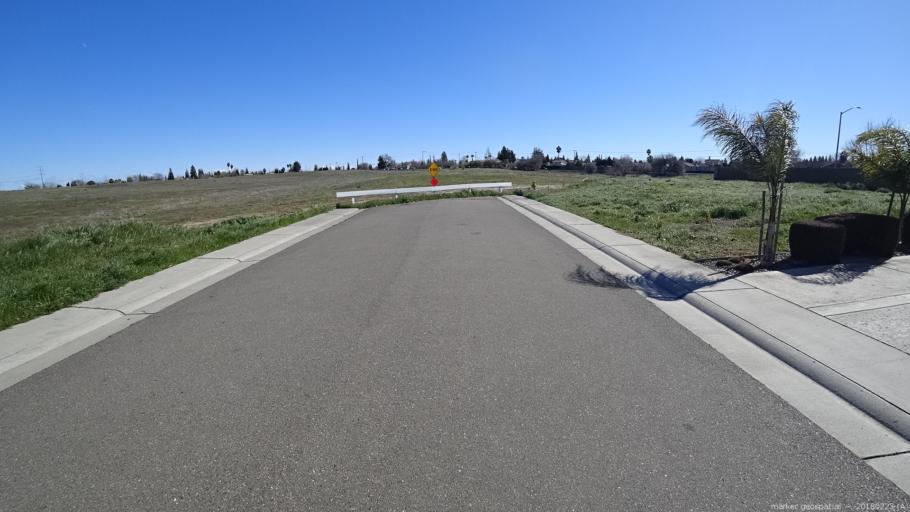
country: US
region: California
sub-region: Sacramento County
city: Antelope
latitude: 38.7057
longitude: -121.3504
